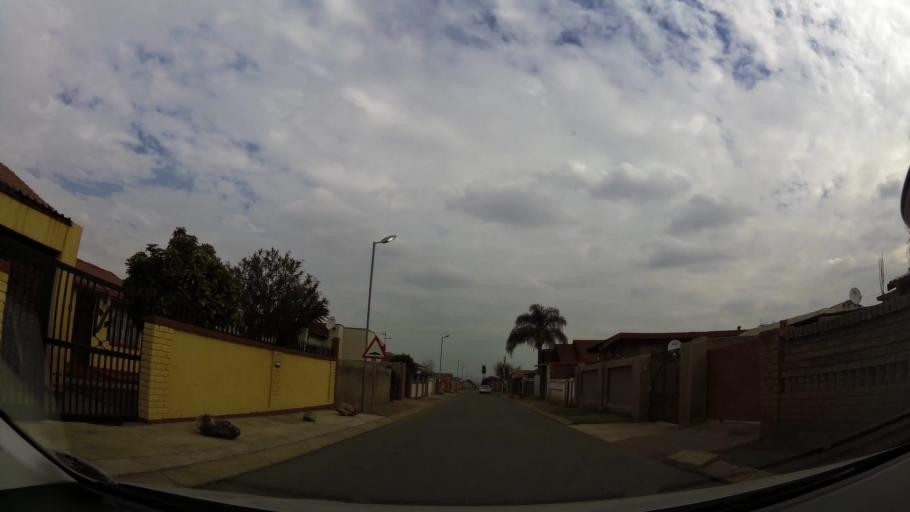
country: ZA
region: Gauteng
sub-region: City of Johannesburg Metropolitan Municipality
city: Soweto
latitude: -26.2655
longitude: 27.8538
